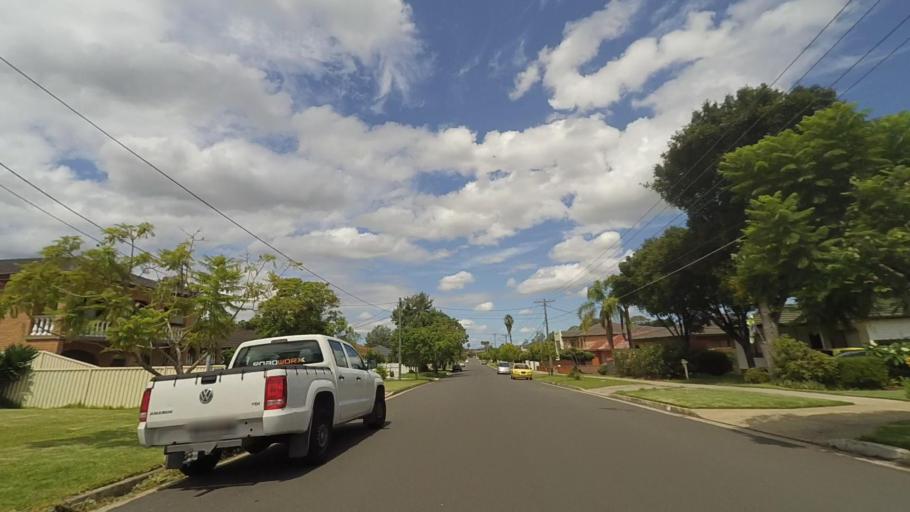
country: AU
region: New South Wales
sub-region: Fairfield
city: Fairfield Heights
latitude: -33.8707
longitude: 150.9423
